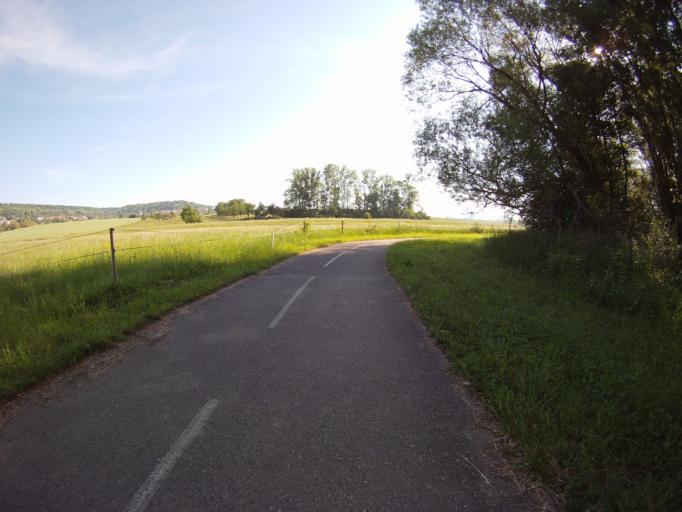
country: FR
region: Lorraine
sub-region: Departement de Meurthe-et-Moselle
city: Eulmont
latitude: 48.7414
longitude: 6.2228
